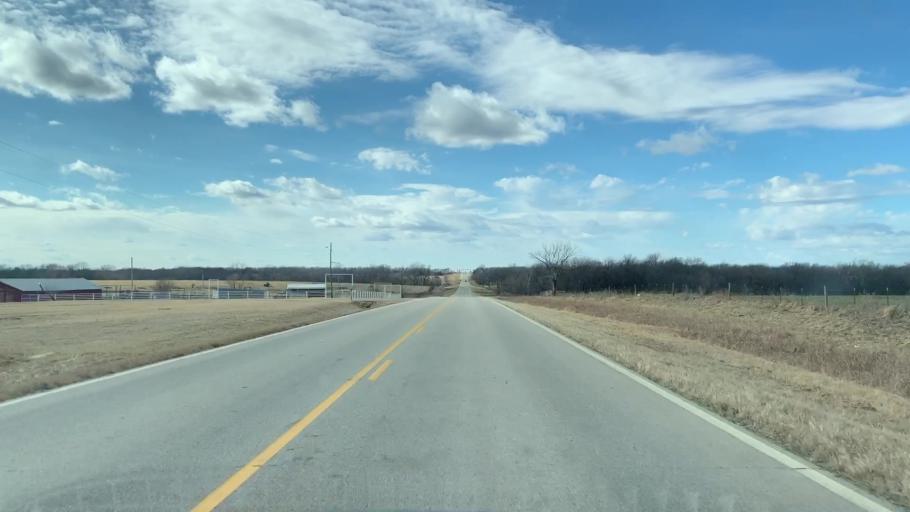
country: US
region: Kansas
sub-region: Neosho County
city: Chanute
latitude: 37.5288
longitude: -95.4547
